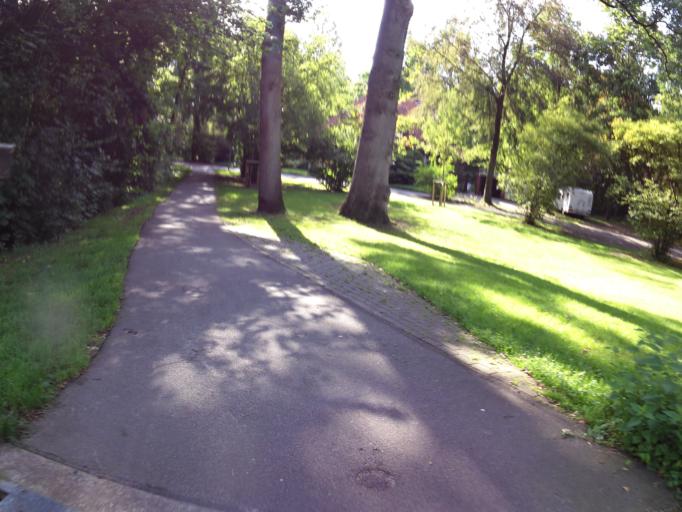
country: DE
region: Lower Saxony
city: Bremervorde
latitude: 53.4806
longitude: 9.1555
